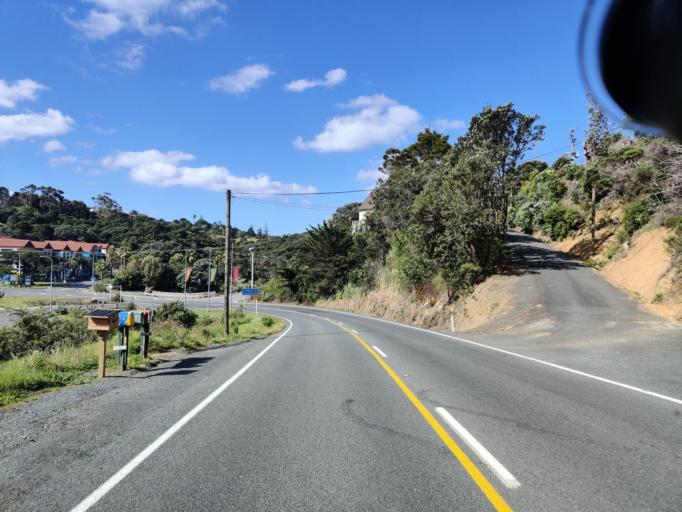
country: NZ
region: Northland
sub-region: Whangarei
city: Ngunguru
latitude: -35.6118
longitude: 174.5243
